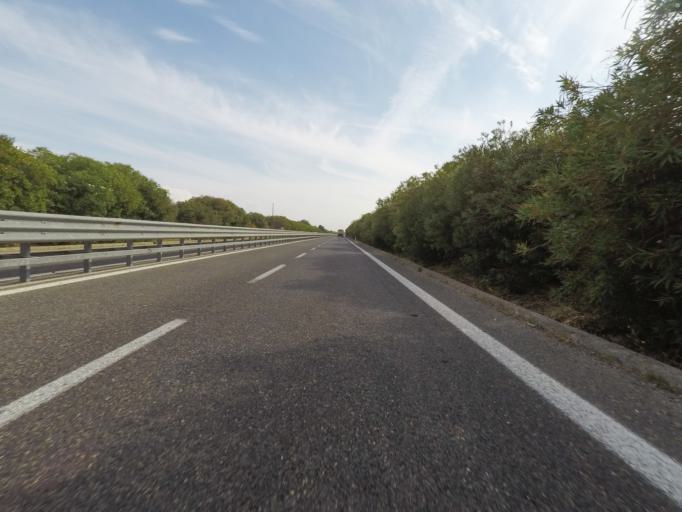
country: IT
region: Latium
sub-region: Provincia di Viterbo
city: Pescia Romana
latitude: 42.3827
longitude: 11.5496
